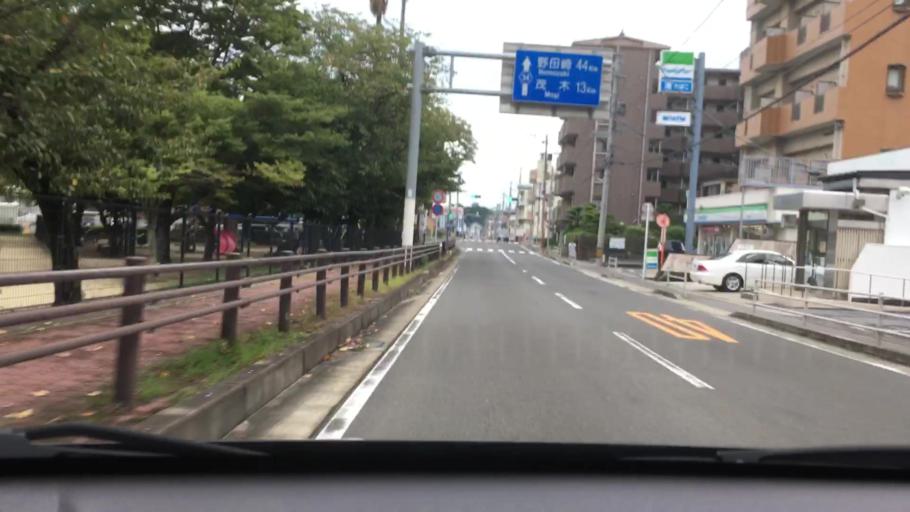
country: JP
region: Nagasaki
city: Nagasaki-shi
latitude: 32.7592
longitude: 129.9420
